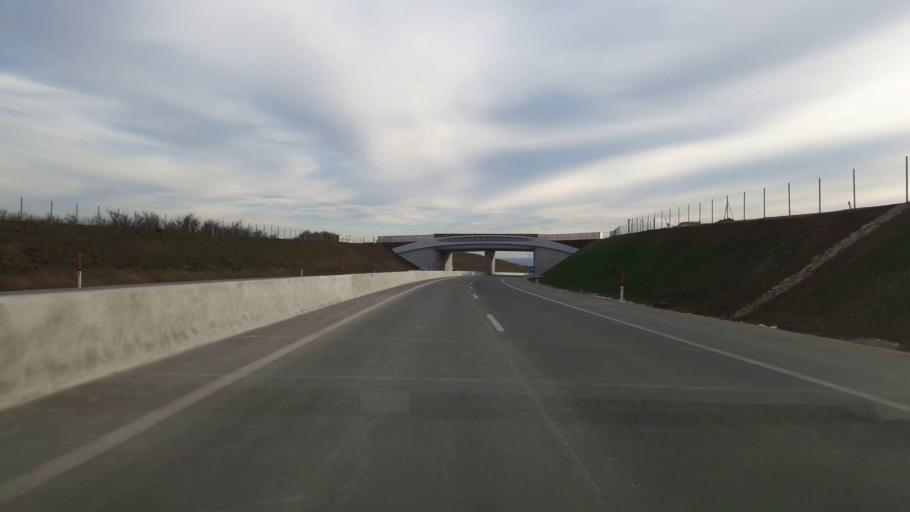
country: AT
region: Lower Austria
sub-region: Politischer Bezirk Mistelbach
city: Herrnbaumgarten
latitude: 48.6972
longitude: 16.6538
